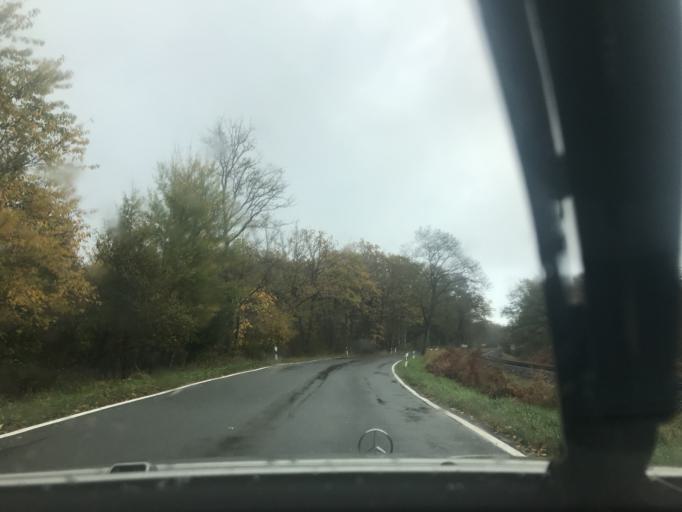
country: DE
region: Mecklenburg-Vorpommern
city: Karlshagen
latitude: 54.1449
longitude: 13.8011
